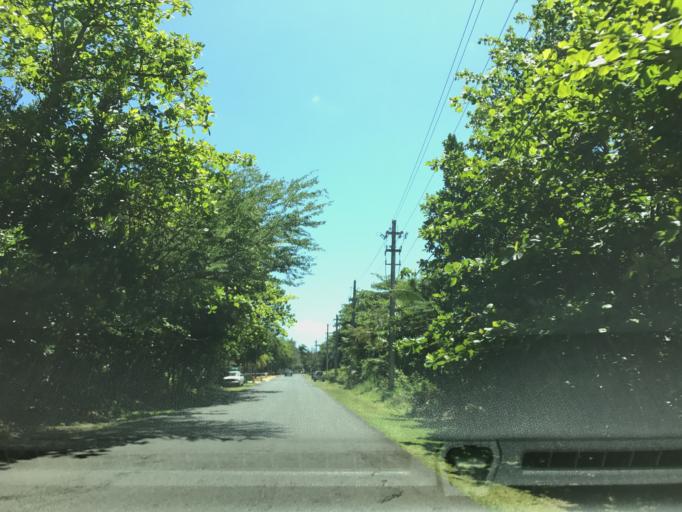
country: PR
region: Rio Grande
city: Palmer
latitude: 18.3957
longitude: -65.7681
